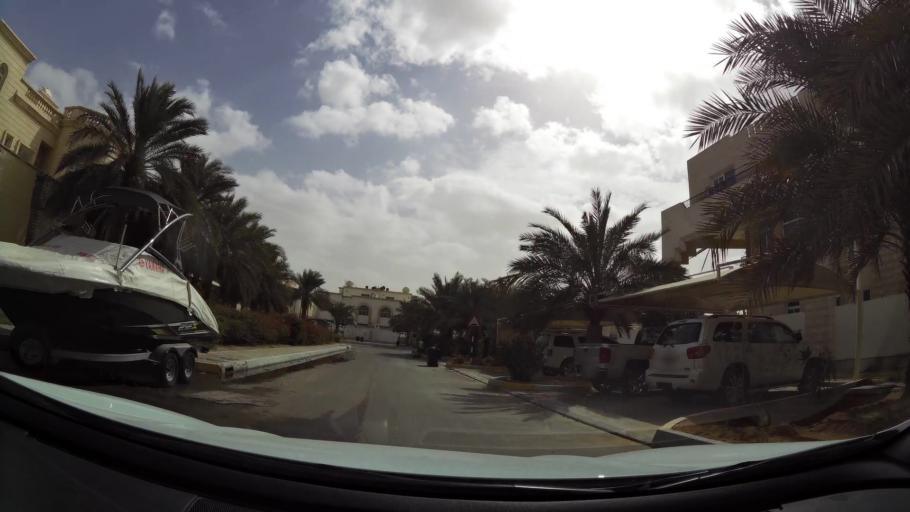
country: AE
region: Abu Dhabi
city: Abu Dhabi
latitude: 24.4053
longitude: 54.4944
